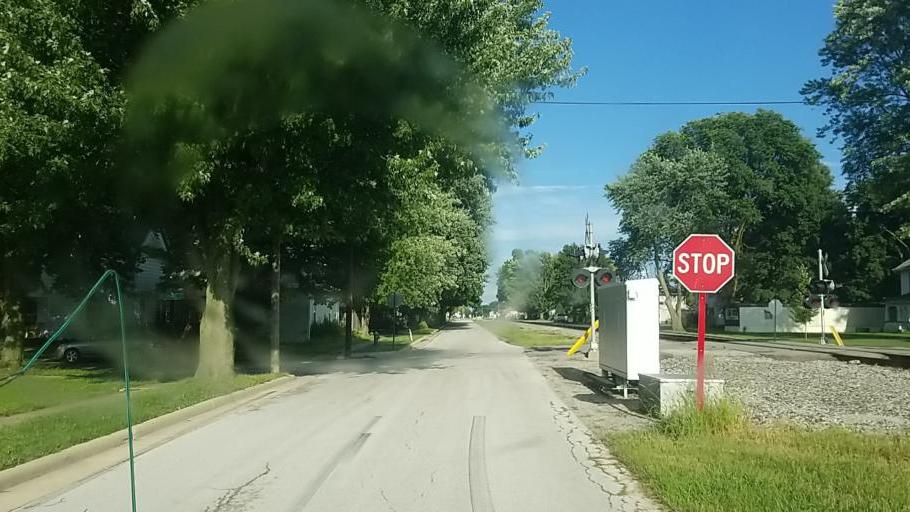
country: US
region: Ohio
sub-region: Wyandot County
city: Upper Sandusky
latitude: 40.8249
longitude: -83.2885
